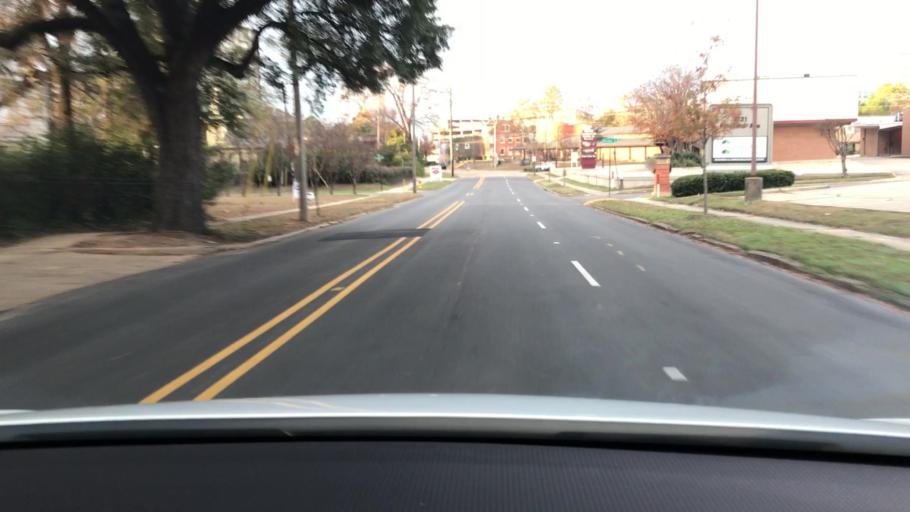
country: US
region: Louisiana
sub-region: Bossier Parish
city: Bossier City
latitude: 32.4914
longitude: -93.7509
